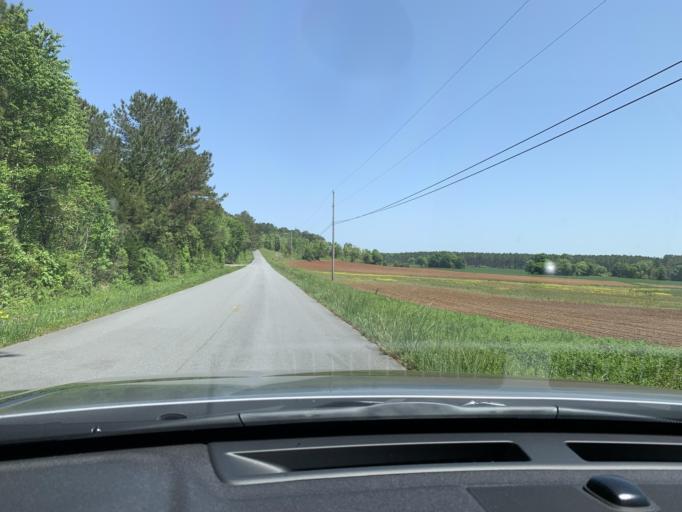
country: US
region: Georgia
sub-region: Polk County
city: Cedartown
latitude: 34.0407
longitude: -85.1905
